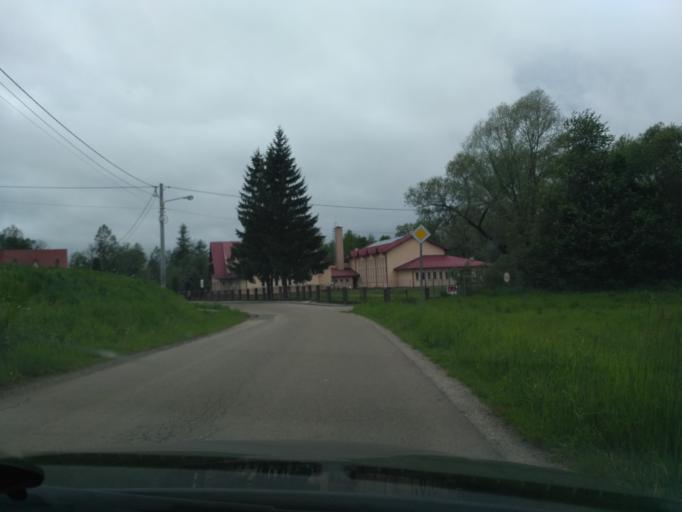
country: PL
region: Subcarpathian Voivodeship
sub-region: Powiat jasielski
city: Brzyska
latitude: 49.8504
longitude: 21.3741
